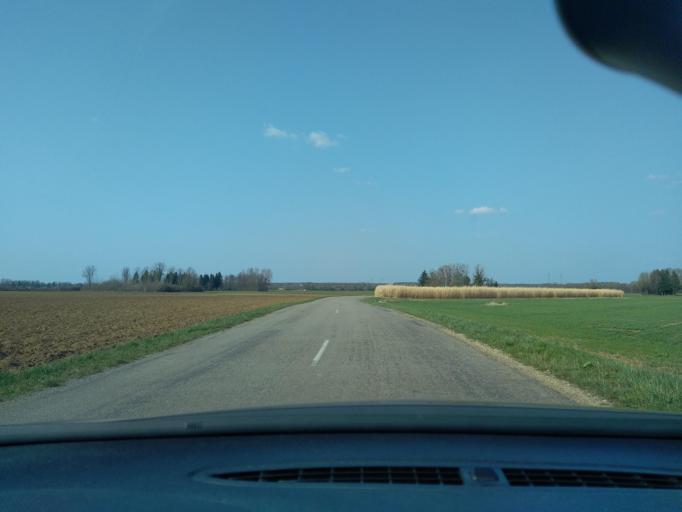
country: FR
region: Franche-Comte
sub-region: Departement du Jura
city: Mont-sous-Vaudrey
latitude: 46.9915
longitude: 5.6060
